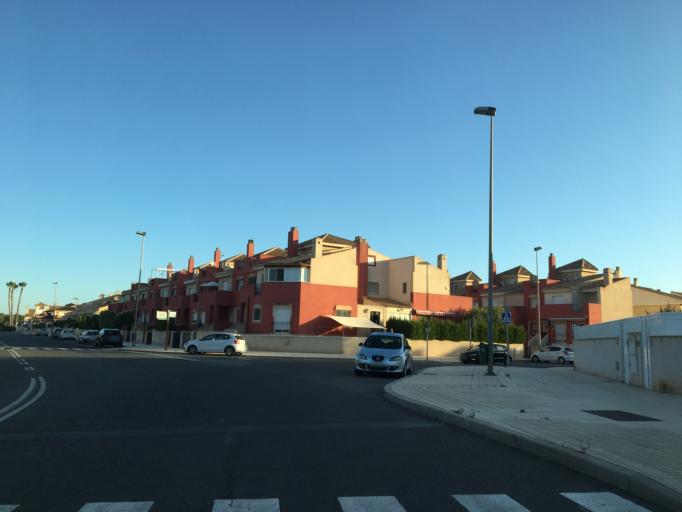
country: ES
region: Murcia
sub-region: Murcia
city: Cartagena
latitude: 37.6530
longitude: -1.0170
